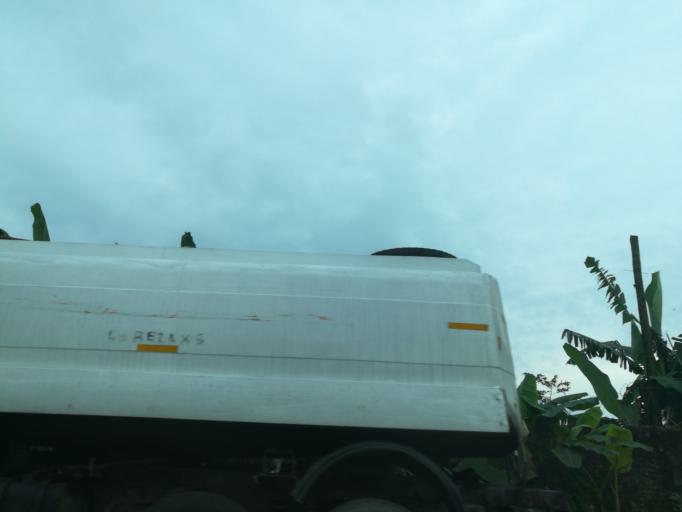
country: NG
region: Rivers
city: Port Harcourt
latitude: 4.8306
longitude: 7.0214
